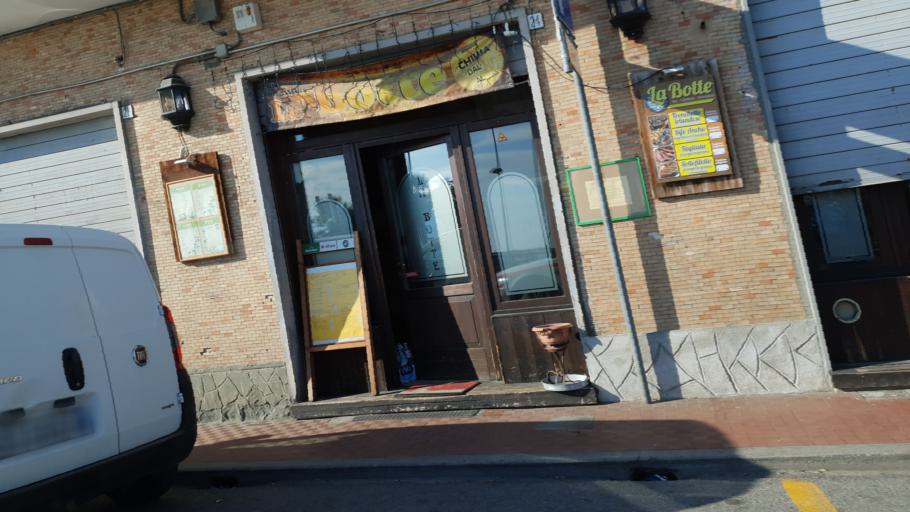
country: IT
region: Liguria
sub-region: Provincia di Savona
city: Vado Ligure
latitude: 44.2762
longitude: 8.4406
